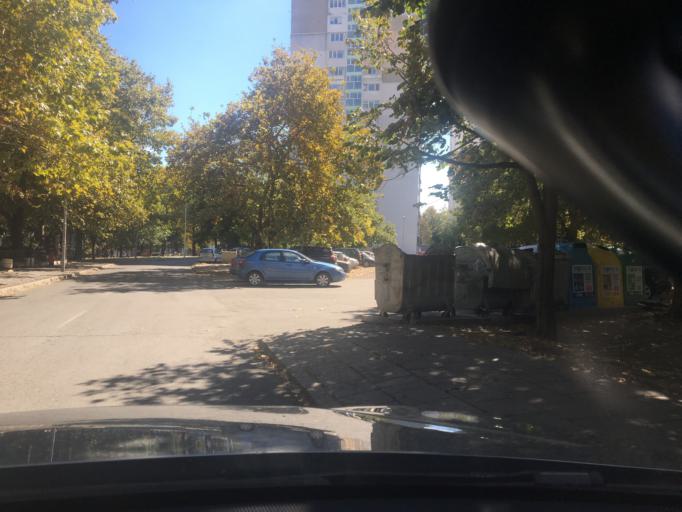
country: BG
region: Burgas
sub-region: Obshtina Burgas
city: Burgas
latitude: 42.5056
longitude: 27.4749
